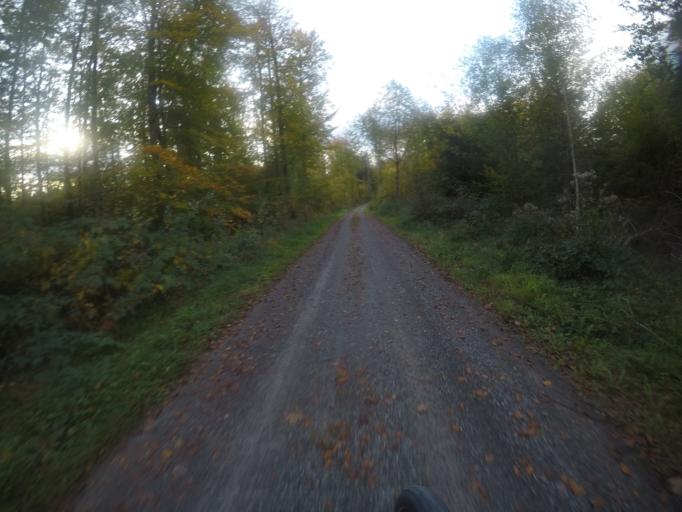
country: DE
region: Baden-Wuerttemberg
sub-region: Regierungsbezirk Stuttgart
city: Weil im Schonbuch
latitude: 48.5955
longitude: 9.0677
